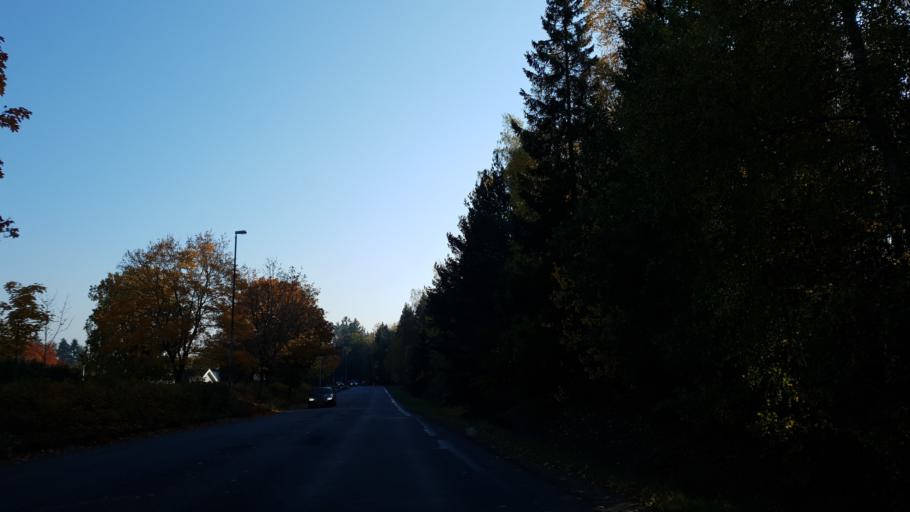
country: SE
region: Stockholm
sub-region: Haninge Kommun
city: Haninge
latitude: 59.1735
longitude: 18.1868
